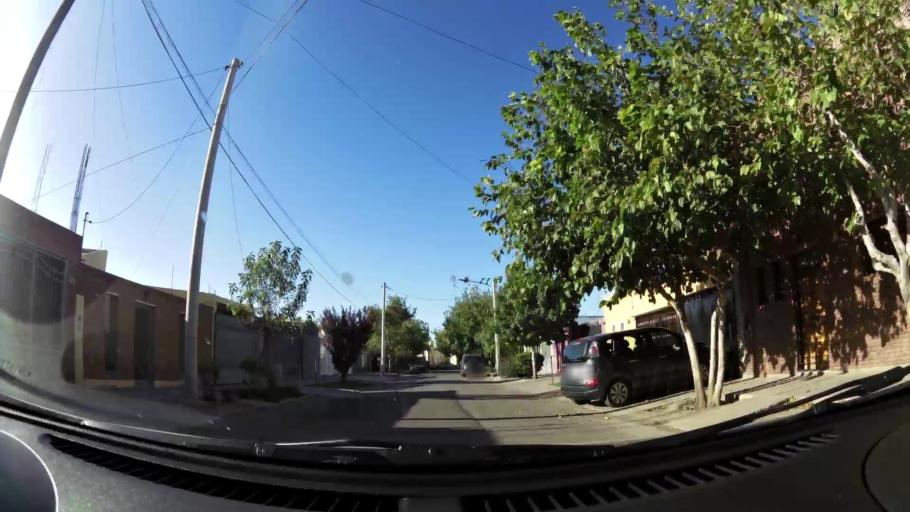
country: AR
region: San Juan
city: Villa Krause
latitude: -31.5599
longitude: -68.5156
